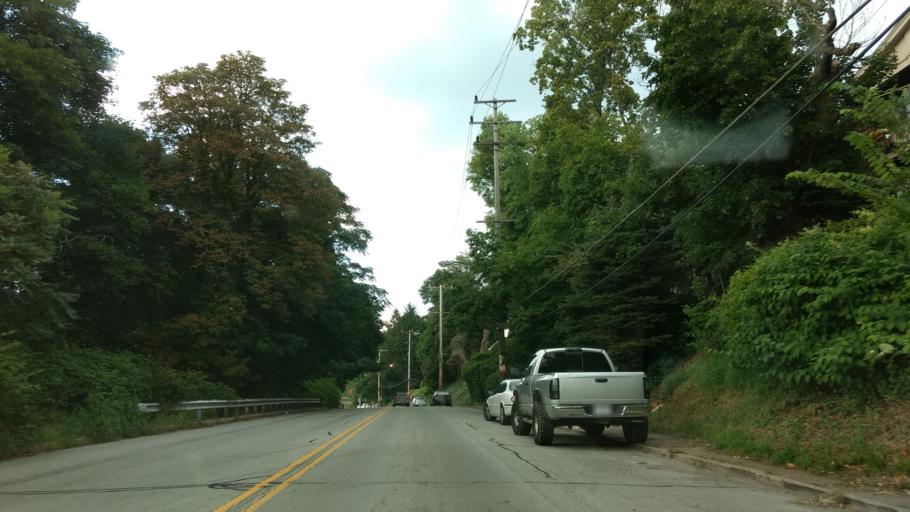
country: US
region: Pennsylvania
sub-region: Allegheny County
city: West View
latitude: 40.4947
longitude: -80.0209
